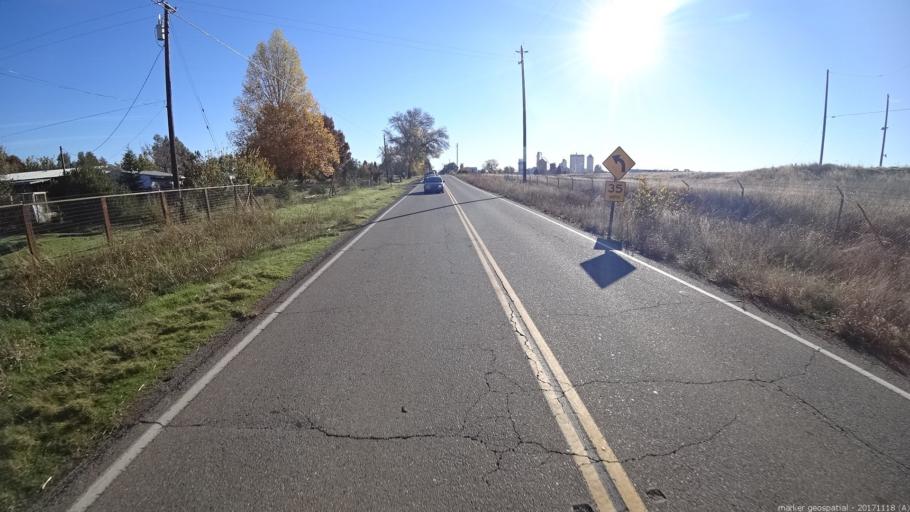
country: US
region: California
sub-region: Shasta County
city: Anderson
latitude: 40.4398
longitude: -122.2741
